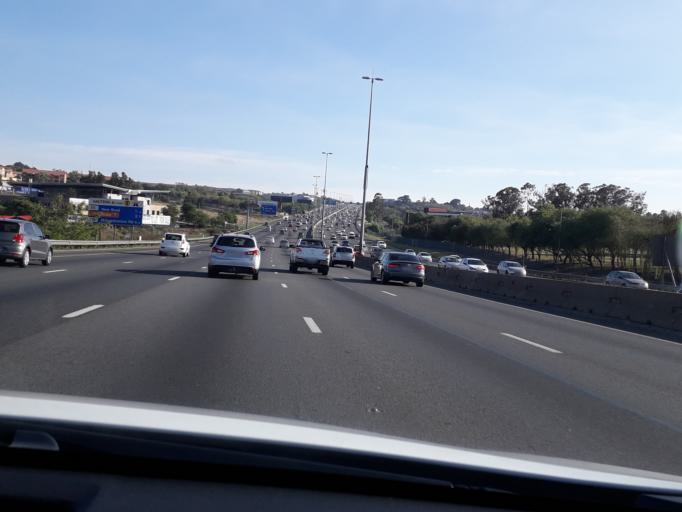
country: ZA
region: Gauteng
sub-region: City of Johannesburg Metropolitan Municipality
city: Midrand
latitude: -25.9972
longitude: 28.1213
